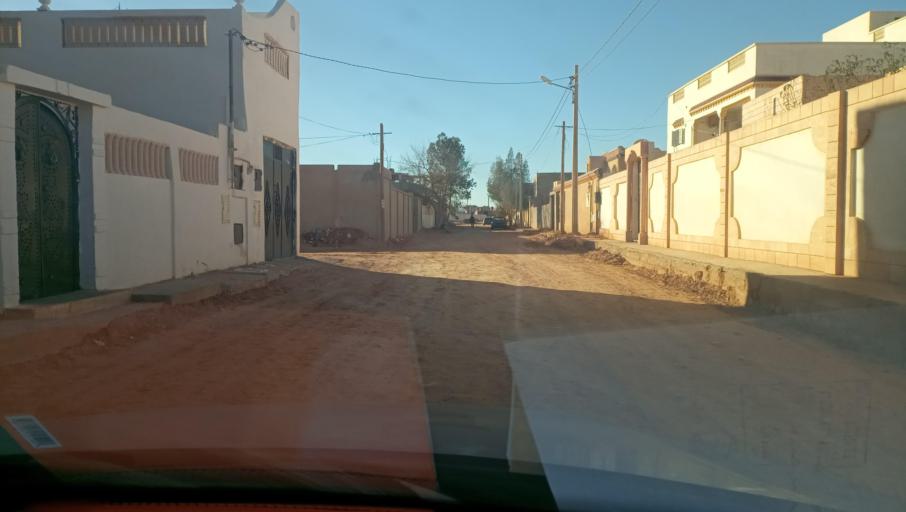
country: TN
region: Tataouine
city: Tataouine
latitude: 32.9874
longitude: 10.4598
